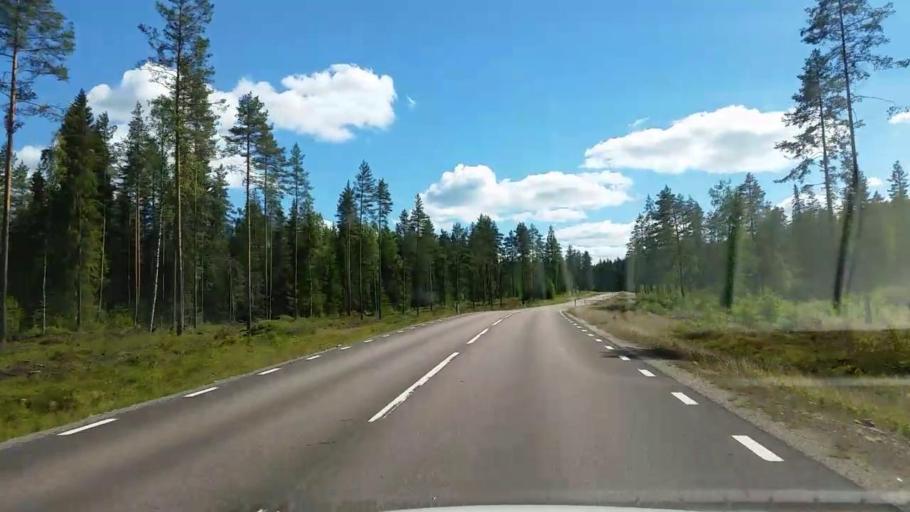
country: SE
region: Dalarna
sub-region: Faluns Kommun
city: Svardsjo
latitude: 60.7810
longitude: 15.7527
